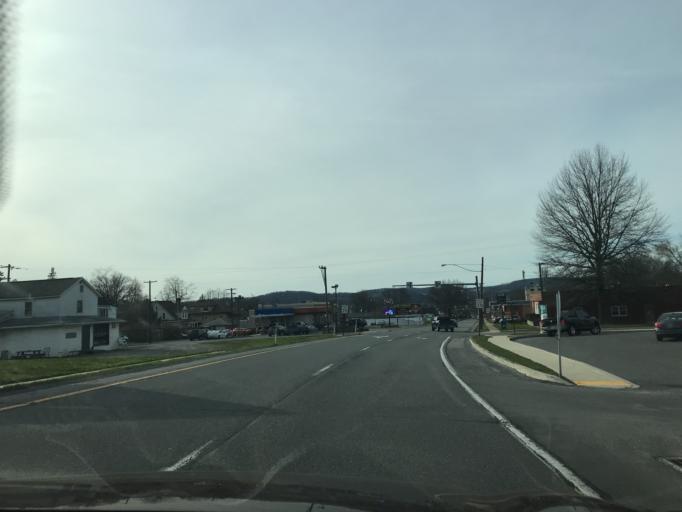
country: US
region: Pennsylvania
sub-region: Lycoming County
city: South Williamsport
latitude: 41.2281
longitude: -76.9897
